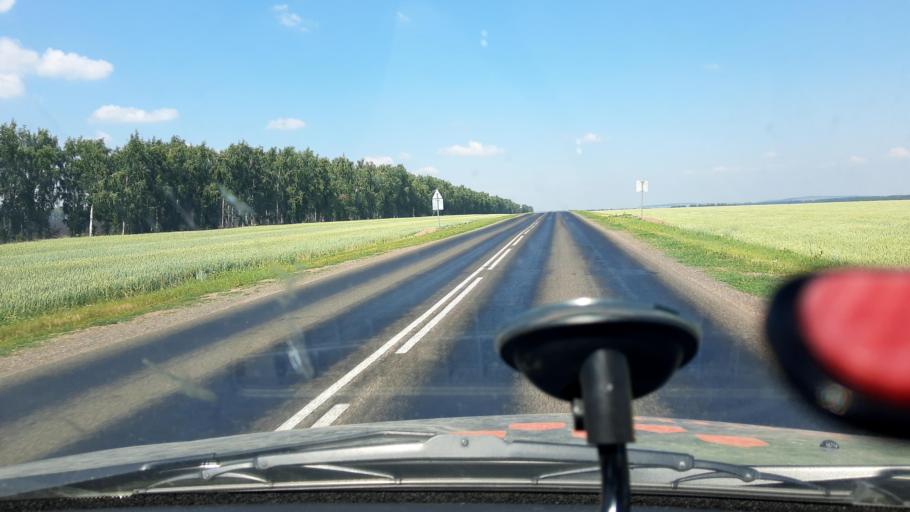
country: RU
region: Bashkortostan
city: Chekmagush
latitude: 55.0752
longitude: 54.6342
